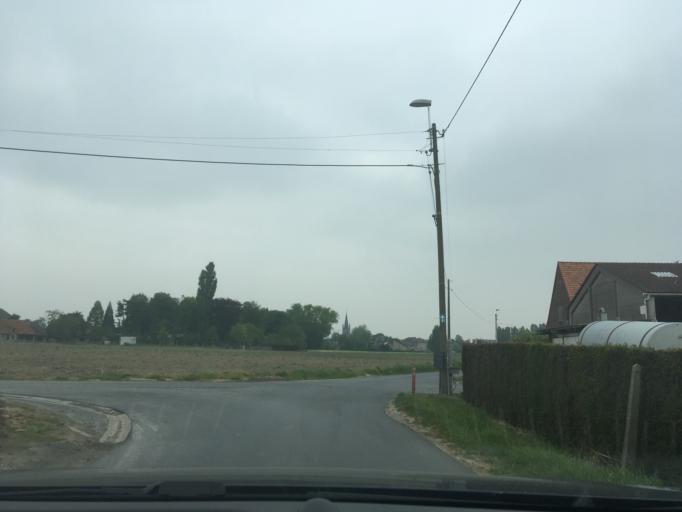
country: BE
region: Flanders
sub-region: Provincie West-Vlaanderen
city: Hooglede
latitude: 50.9996
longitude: 3.1051
